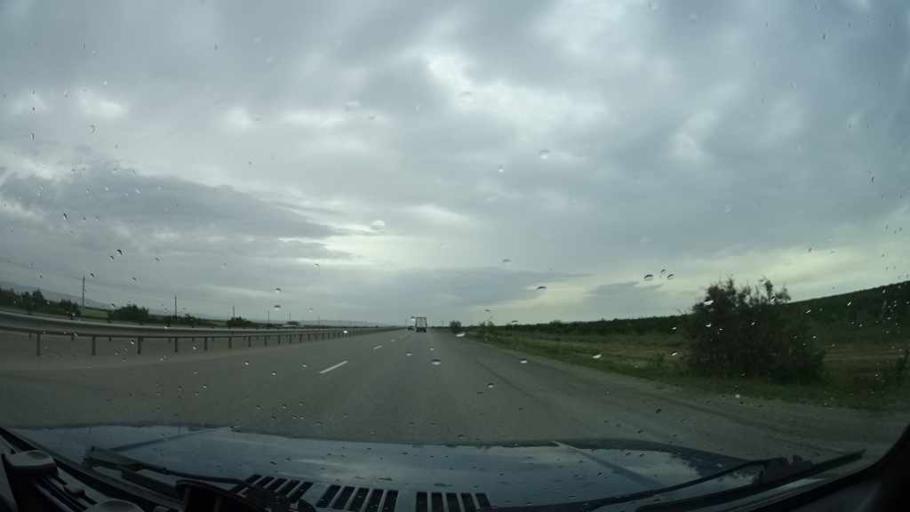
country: AZ
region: Goranboy
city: Goranboy
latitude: 40.6452
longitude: 46.7348
